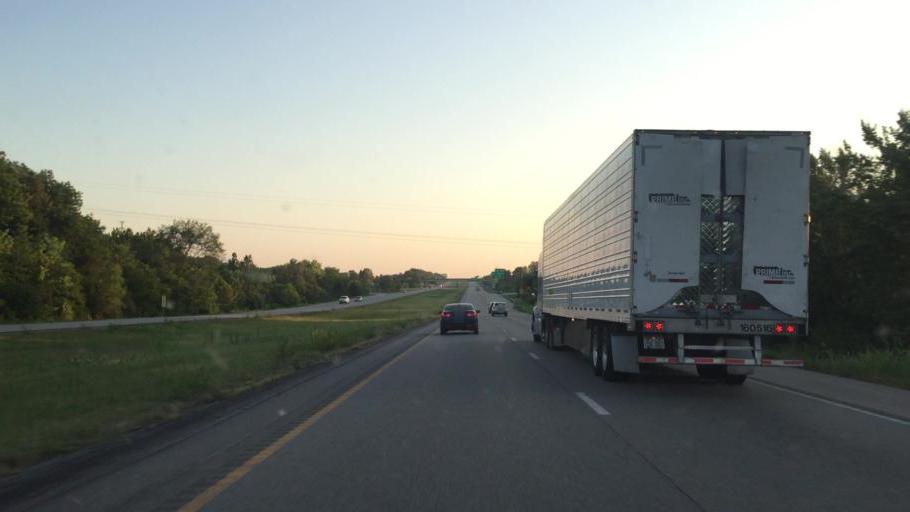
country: US
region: Missouri
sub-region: Clay County
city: Pleasant Valley
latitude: 39.2802
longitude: -94.5101
